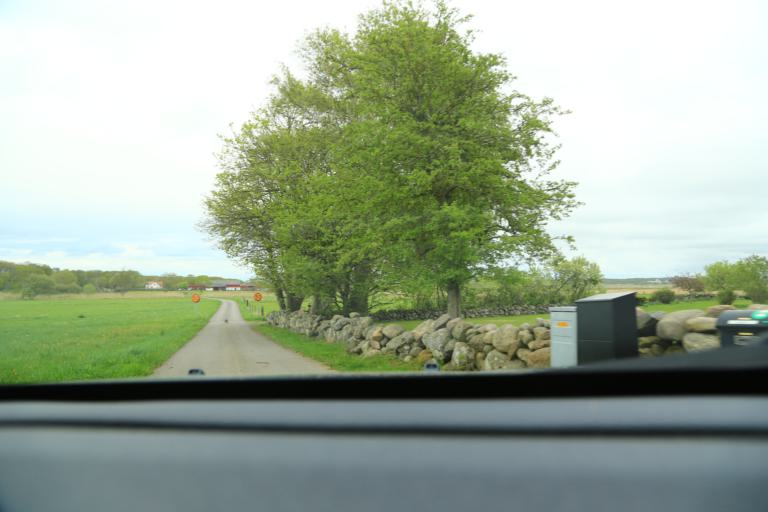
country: SE
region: Halland
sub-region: Varbergs Kommun
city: Varberg
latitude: 57.1386
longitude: 12.2279
